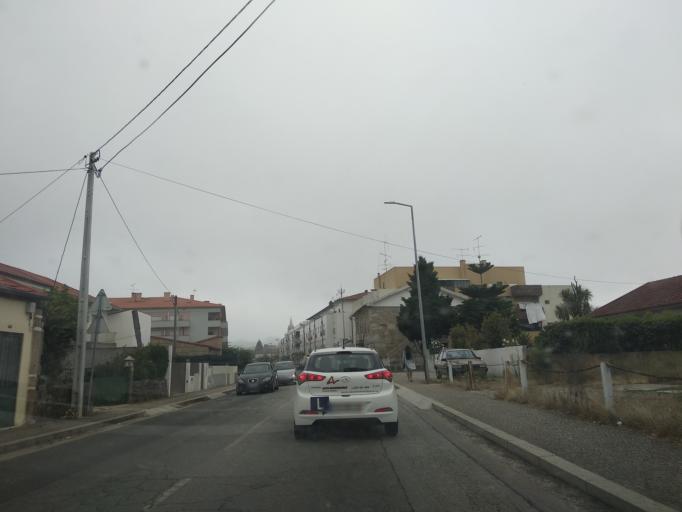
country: PT
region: Braga
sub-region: Vila Verde
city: Vila Verde
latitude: 41.6439
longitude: -8.4354
